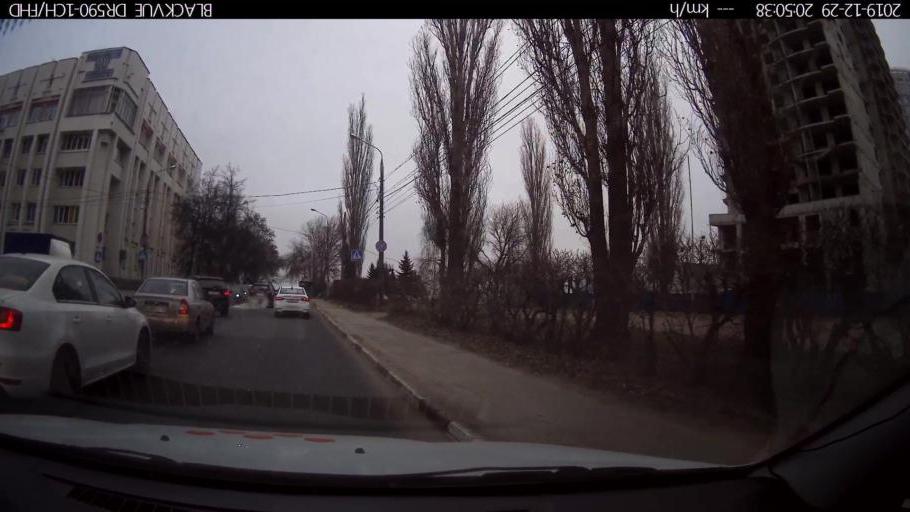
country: RU
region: Nizjnij Novgorod
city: Nizhniy Novgorod
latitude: 56.3186
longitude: 44.0324
